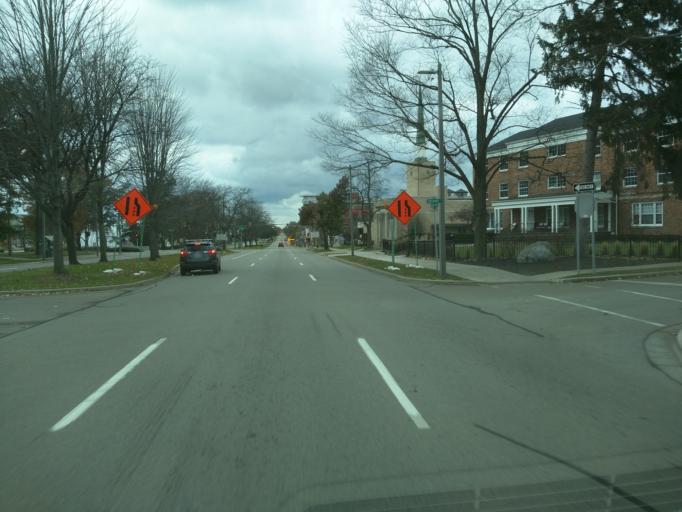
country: US
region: Michigan
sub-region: Ingham County
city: East Lansing
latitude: 42.7325
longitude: -84.4736
